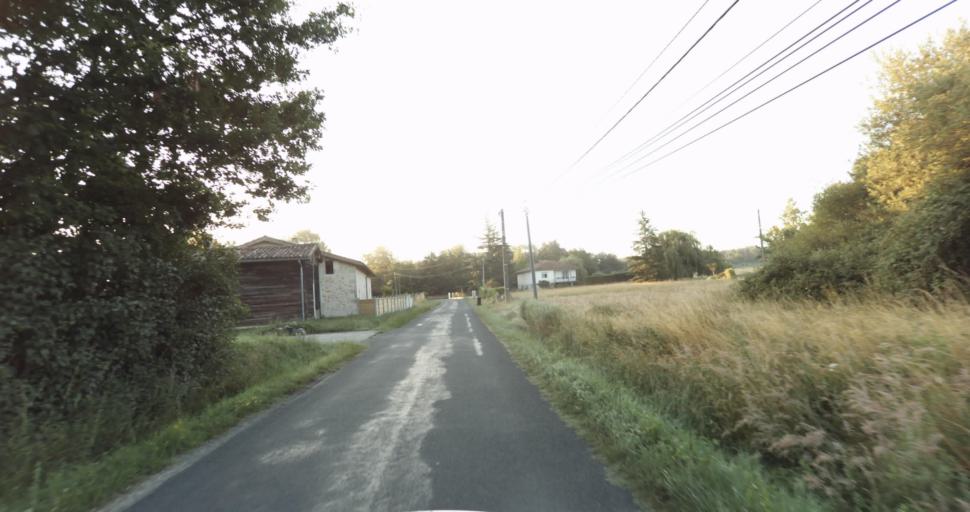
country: FR
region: Aquitaine
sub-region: Departement de la Gironde
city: Bazas
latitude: 44.4175
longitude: -0.2148
